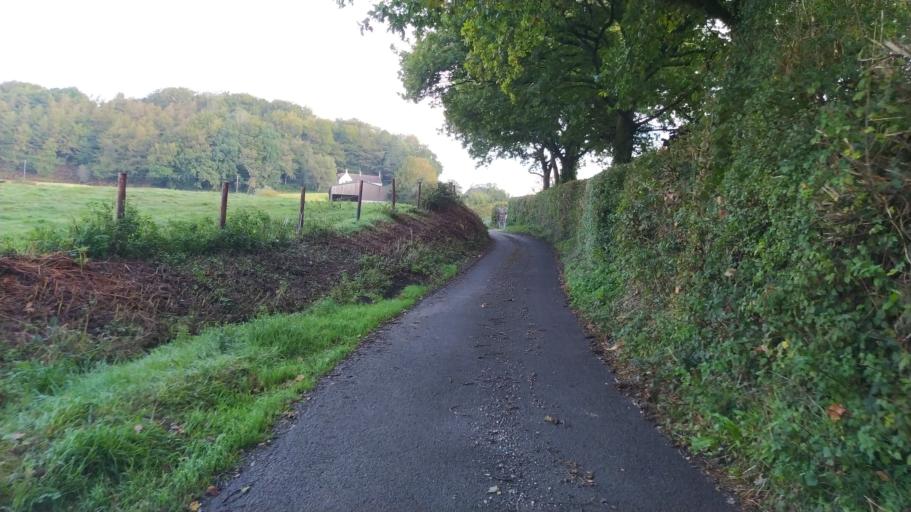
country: GB
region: England
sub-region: Dorset
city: Shaftesbury
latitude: 51.0263
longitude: -2.1348
